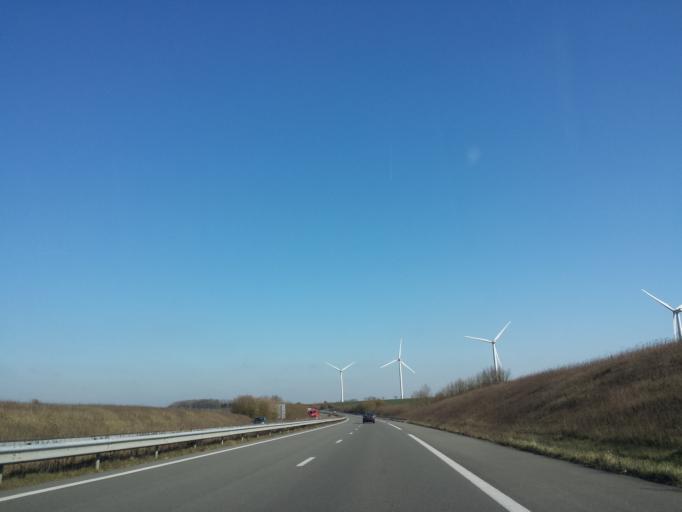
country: FR
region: Picardie
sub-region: Departement de l'Oise
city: Breteuil
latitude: 49.6881
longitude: 2.2259
